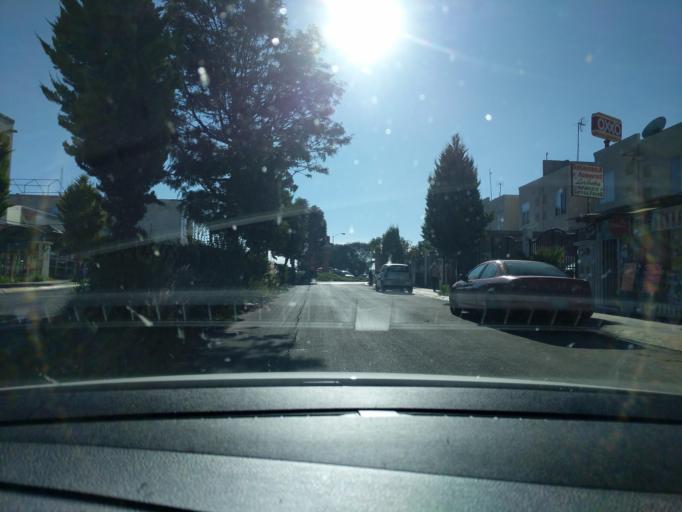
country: MX
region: Puebla
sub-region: Huejotzingo
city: Los Encinos
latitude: 19.1770
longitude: -98.3916
